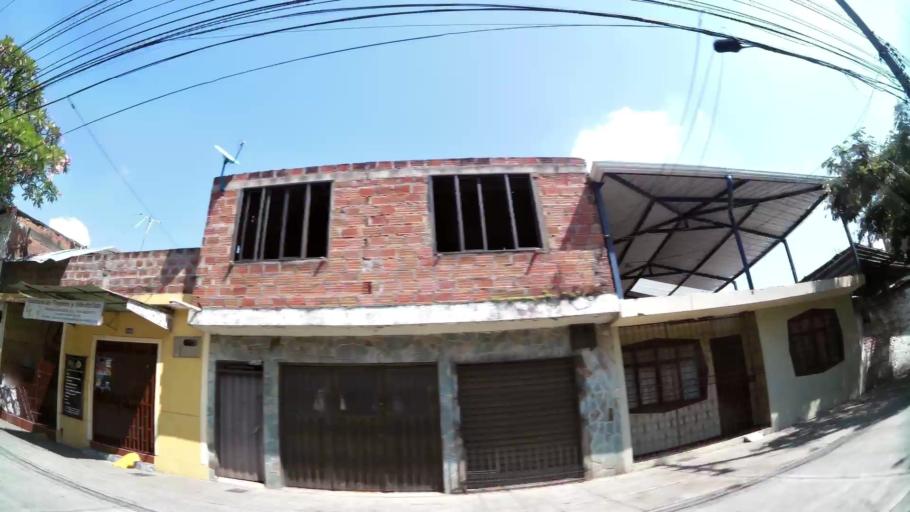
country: CO
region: Valle del Cauca
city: Cali
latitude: 3.4184
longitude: -76.5267
